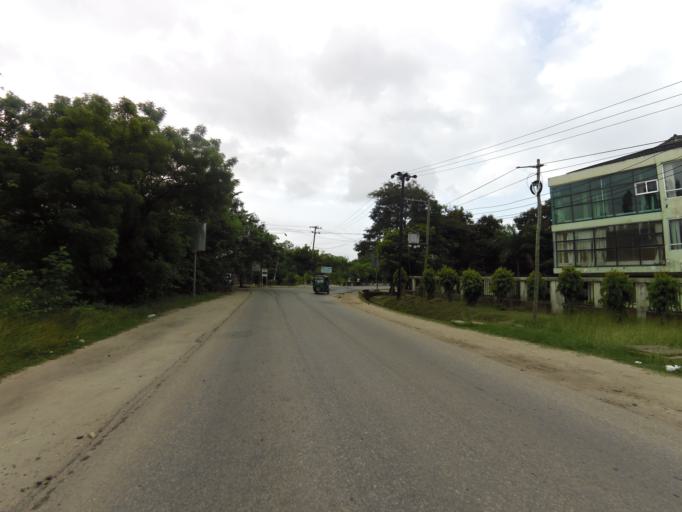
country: TZ
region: Dar es Salaam
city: Magomeni
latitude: -6.7697
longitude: 39.2477
